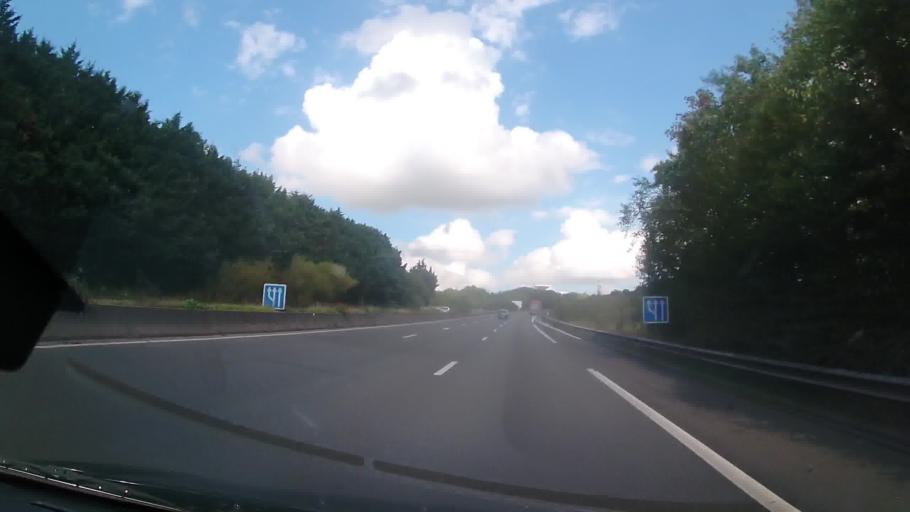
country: FR
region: Nord-Pas-de-Calais
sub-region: Departement du Pas-de-Calais
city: Wimille
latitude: 50.7636
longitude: 1.6372
